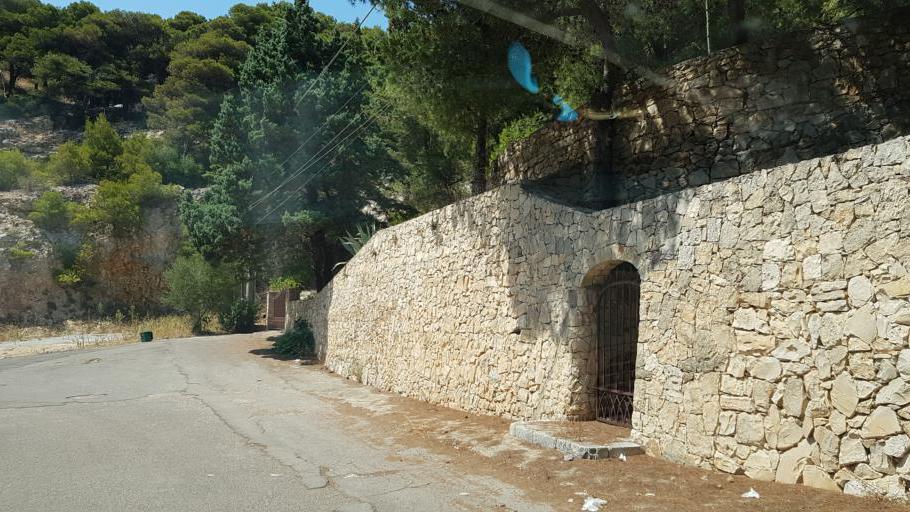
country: IT
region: Apulia
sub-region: Provincia di Lecce
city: Nardo
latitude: 40.1429
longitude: 17.9802
